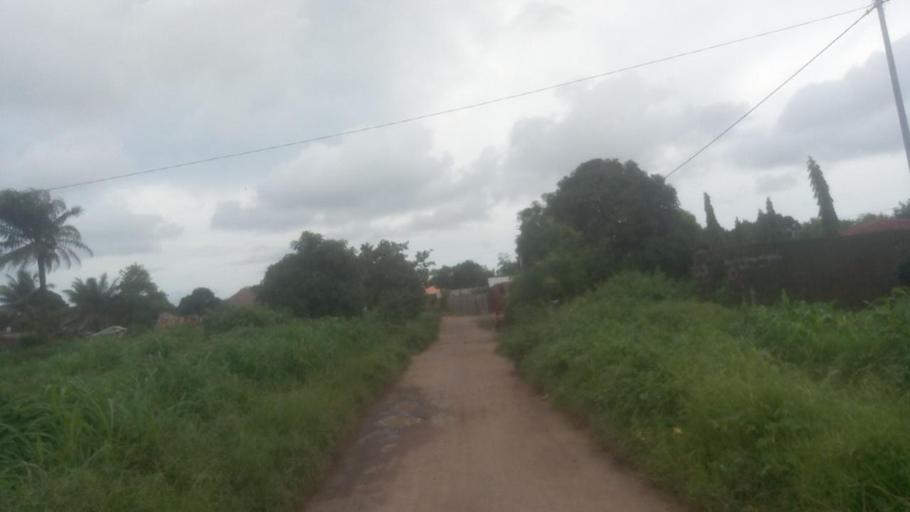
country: SL
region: Northern Province
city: Masoyila
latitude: 8.6072
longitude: -13.1905
